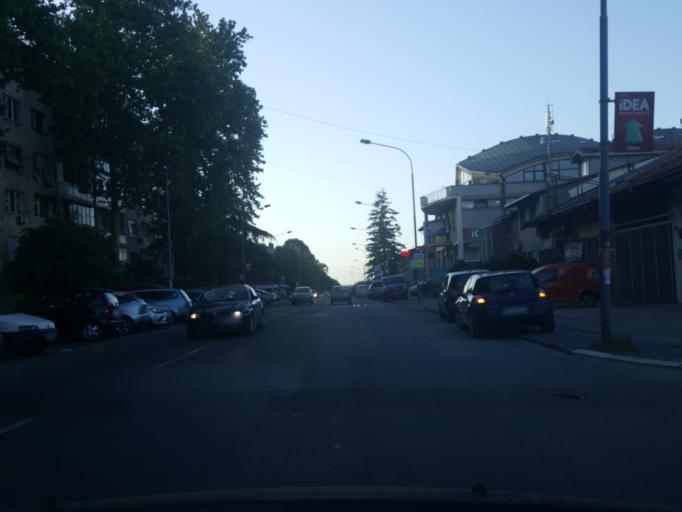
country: RS
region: Central Serbia
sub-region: Belgrade
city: Palilula
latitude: 44.8042
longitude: 20.5251
